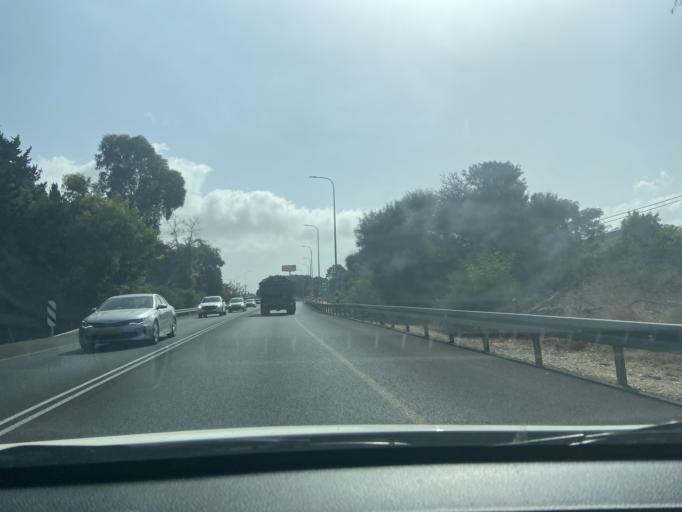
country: IL
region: Northern District
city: Nahariya
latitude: 33.0362
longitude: 35.1050
